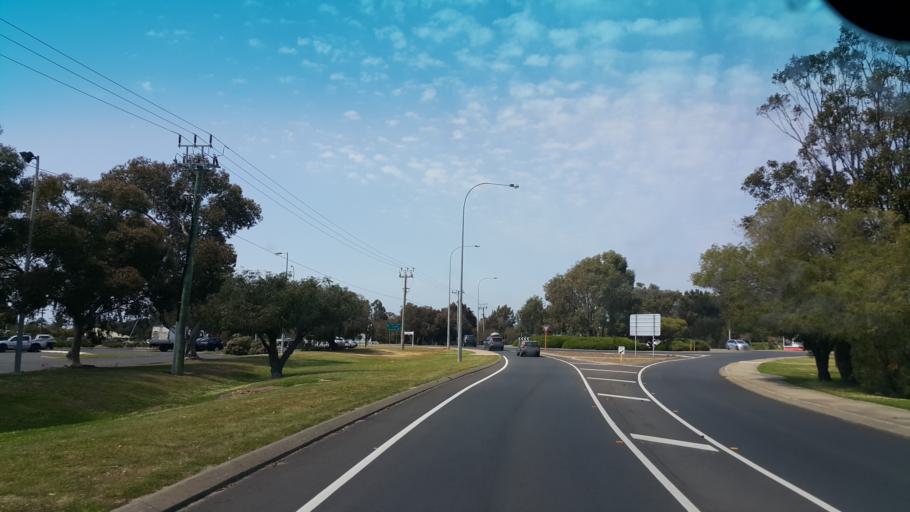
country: AU
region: Western Australia
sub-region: Busselton
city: Dunsborough
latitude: -33.6176
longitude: 115.1063
